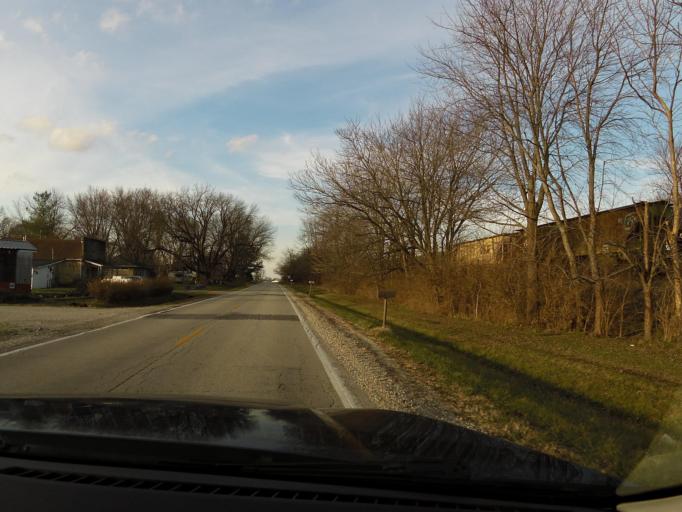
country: US
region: Illinois
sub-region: Fayette County
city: Vandalia
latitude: 38.9448
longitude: -89.1654
